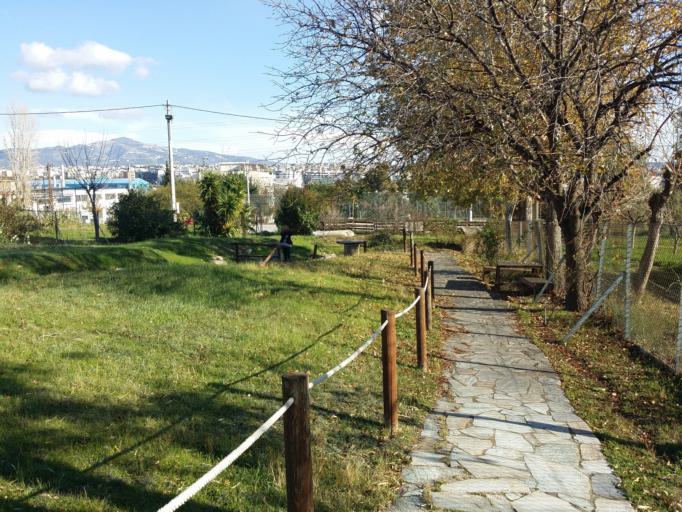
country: GR
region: Attica
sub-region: Nomarchia Dytikis Attikis
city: Zefyri
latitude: 38.0587
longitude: 23.7387
